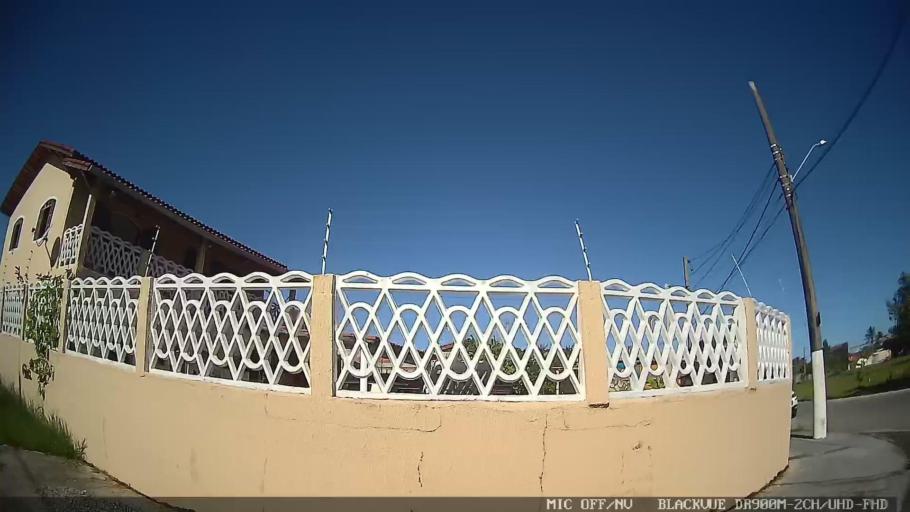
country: BR
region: Sao Paulo
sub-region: Itanhaem
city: Itanhaem
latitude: -24.2082
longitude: -46.8479
